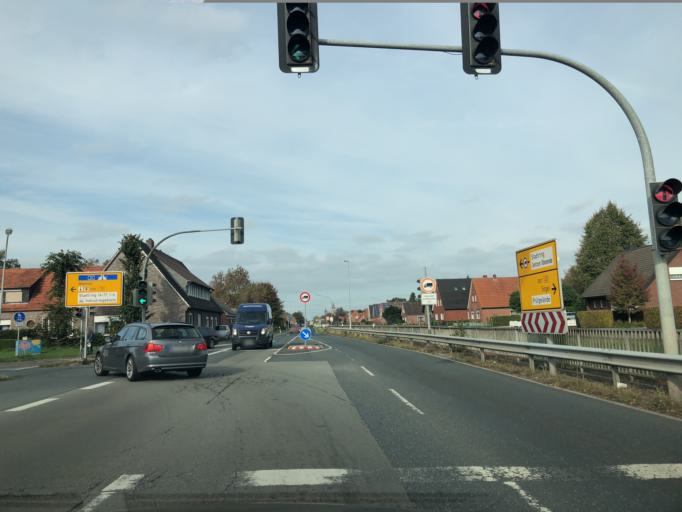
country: DE
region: Lower Saxony
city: Papenburg
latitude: 53.0632
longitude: 7.4502
